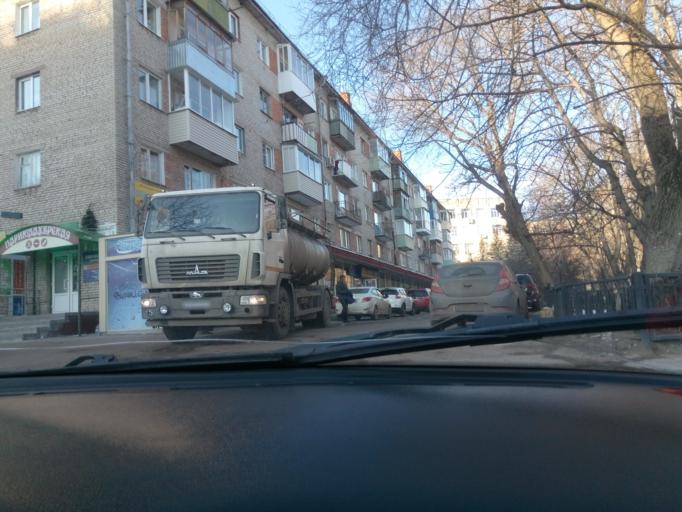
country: RU
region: Tula
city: Mendeleyevskiy
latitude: 54.1712
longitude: 37.5747
